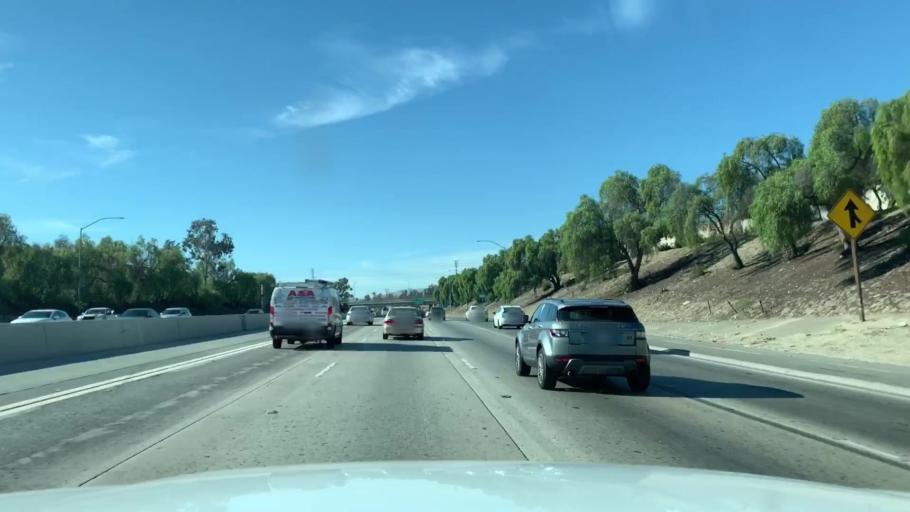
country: US
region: California
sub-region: Los Angeles County
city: North Hollywood
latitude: 34.2275
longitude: -118.3900
